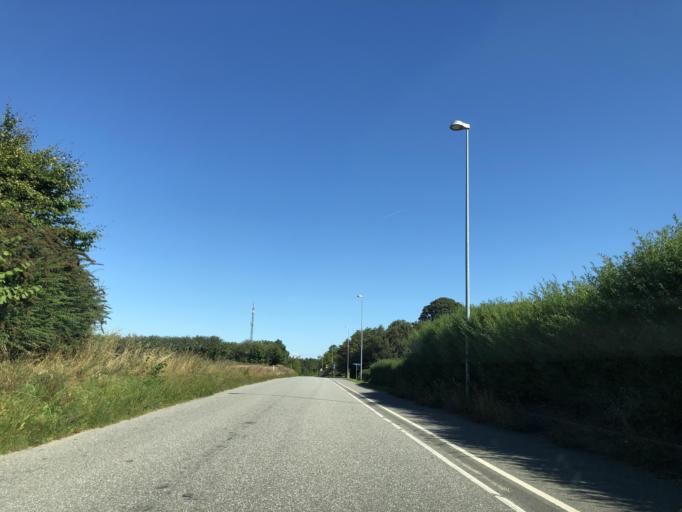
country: DK
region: North Denmark
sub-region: Mariagerfjord Kommune
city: Hobro
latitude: 56.6378
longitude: 9.7706
